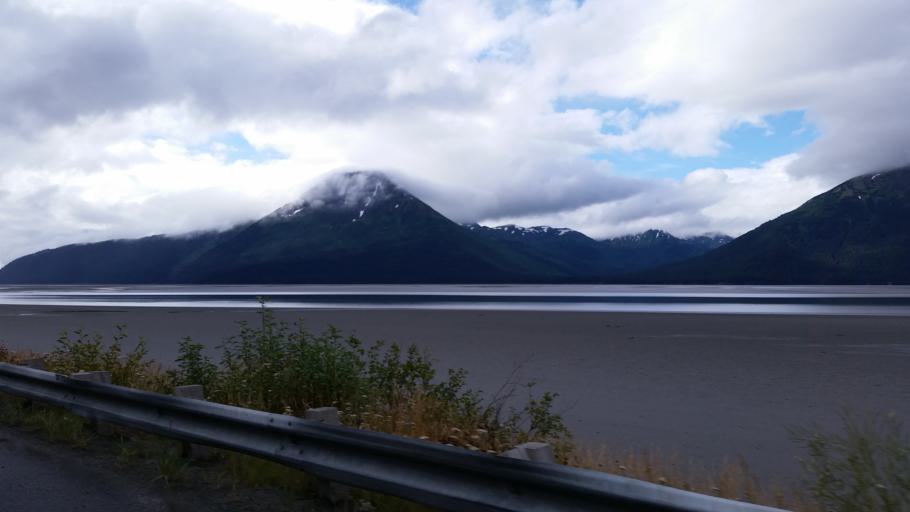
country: US
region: Alaska
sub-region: Anchorage Municipality
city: Girdwood
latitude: 60.9225
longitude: -149.1394
